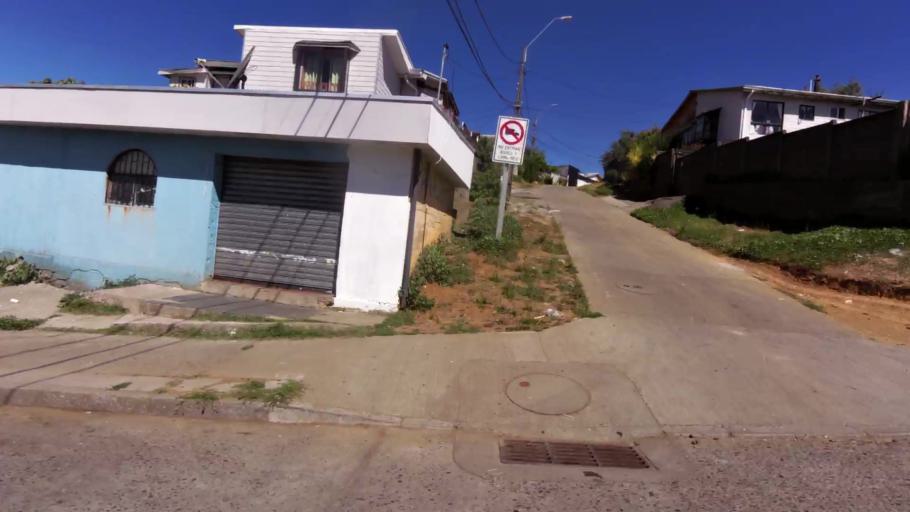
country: CL
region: Biobio
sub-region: Provincia de Concepcion
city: Penco
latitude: -36.7255
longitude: -72.9857
